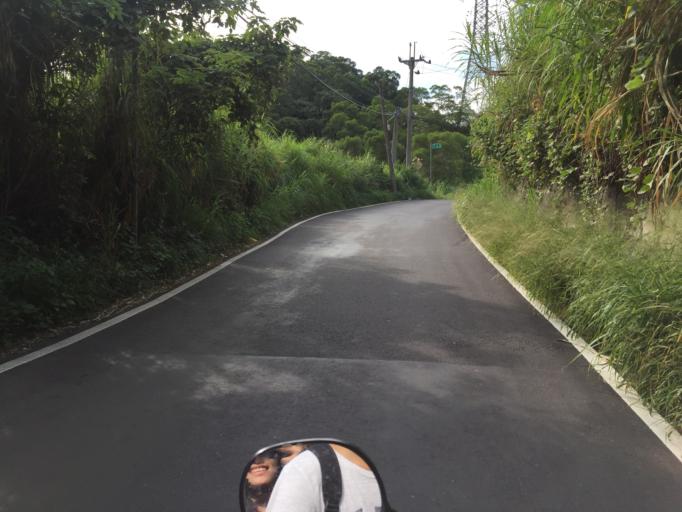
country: TW
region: Taiwan
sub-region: Hsinchu
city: Hsinchu
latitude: 24.7661
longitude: 120.9402
